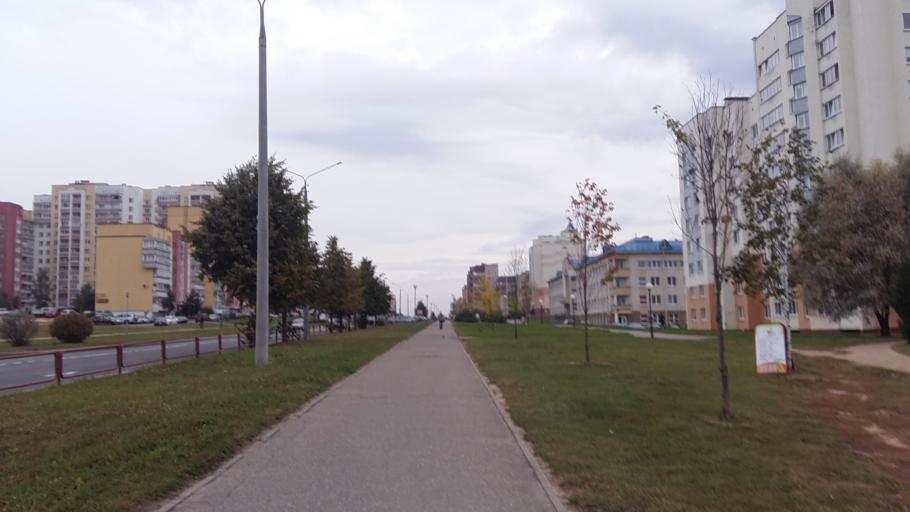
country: BY
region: Grodnenskaya
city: Hrodna
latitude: 53.7085
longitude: 23.8498
